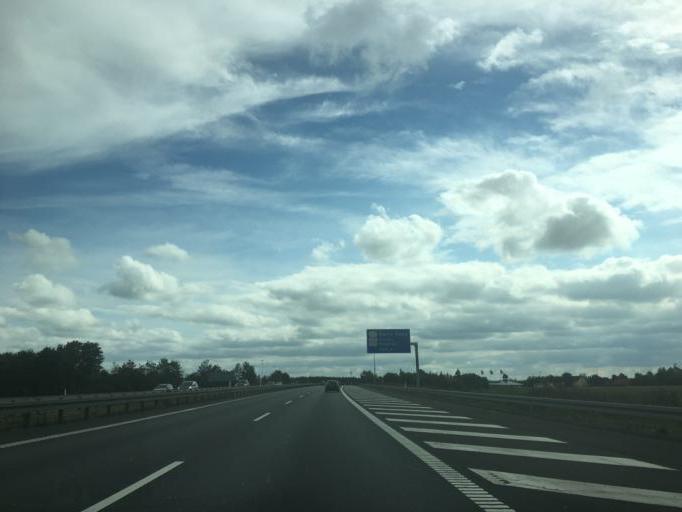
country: DK
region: South Denmark
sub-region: Middelfart Kommune
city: Norre Aby
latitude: 55.4724
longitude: 9.8926
